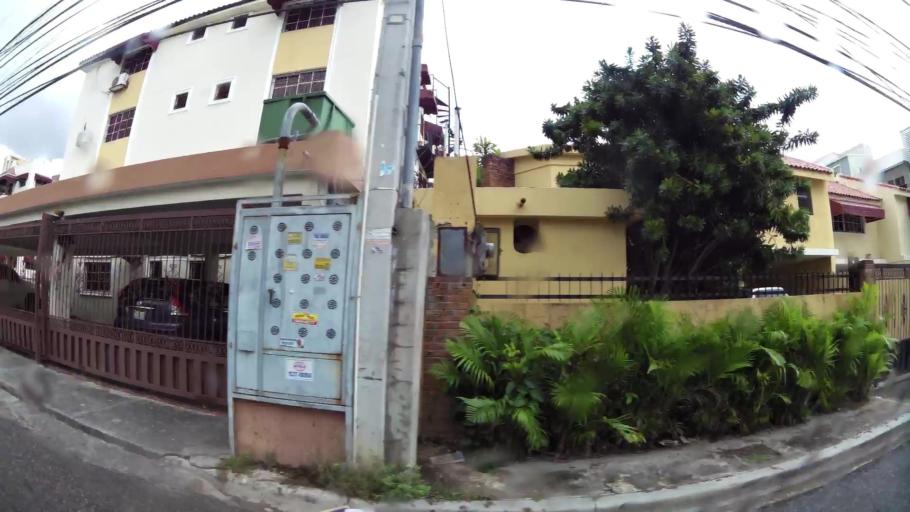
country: DO
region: Nacional
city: La Agustina
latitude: 18.4993
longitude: -69.9352
